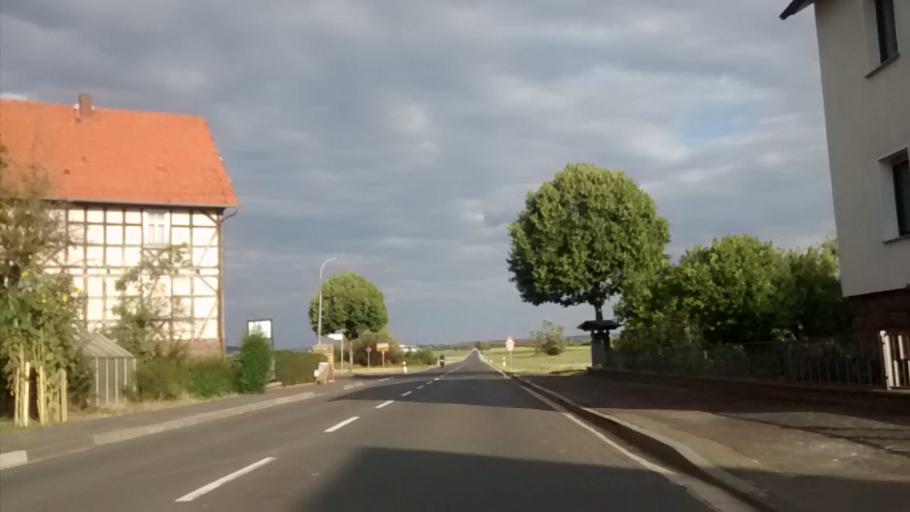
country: DE
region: Hesse
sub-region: Regierungsbezirk Giessen
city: Kirchhain
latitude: 50.8431
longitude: 8.8706
